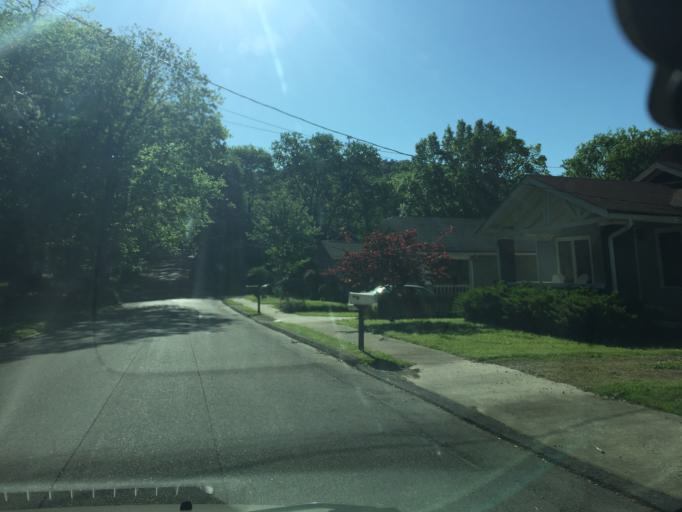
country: US
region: Tennessee
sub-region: Hamilton County
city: Lookout Mountain
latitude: 34.9915
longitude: -85.3291
